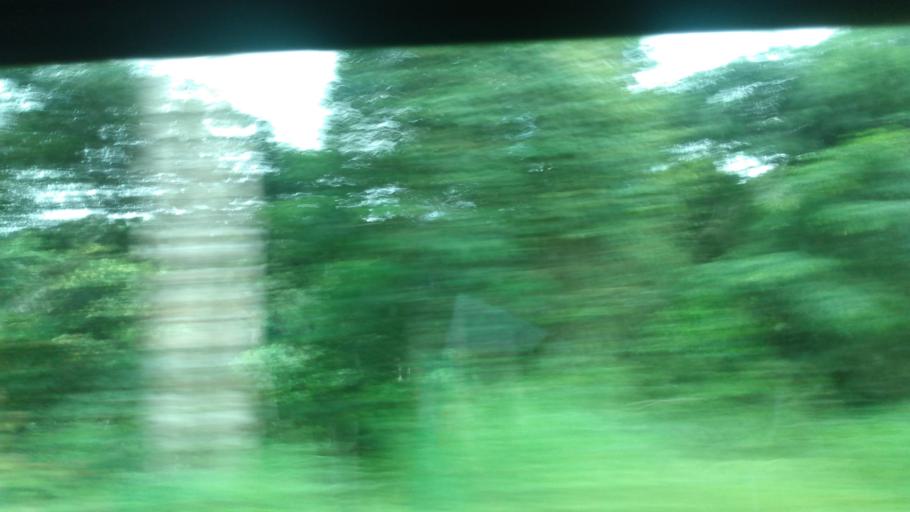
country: BR
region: Pernambuco
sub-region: Maraial
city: Maraial
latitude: -8.7820
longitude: -35.9107
